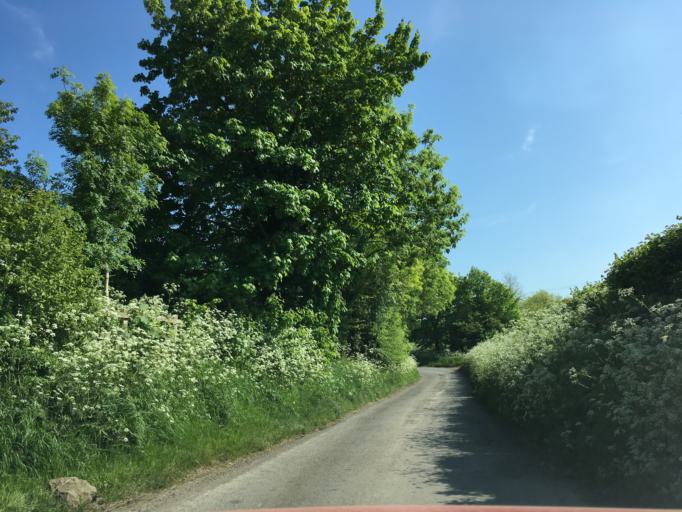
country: GB
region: England
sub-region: Gloucestershire
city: Dursley
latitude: 51.7193
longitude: -2.3833
